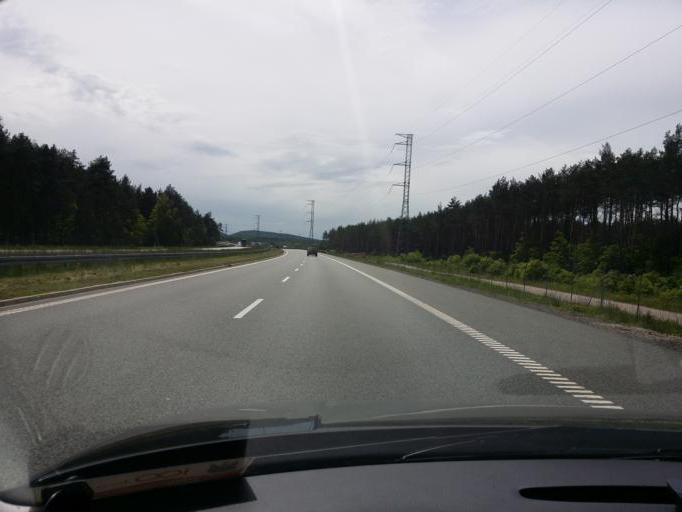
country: PL
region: Swietokrzyskie
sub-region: Powiat kielecki
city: Miedziana Gora
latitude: 50.8941
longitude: 20.5300
